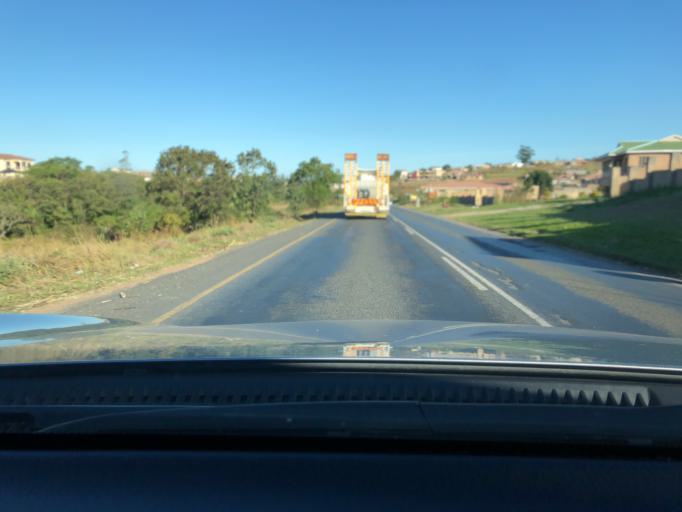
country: ZA
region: KwaZulu-Natal
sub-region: eThekwini Metropolitan Municipality
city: Umkomaas
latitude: -29.9995
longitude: 30.7992
